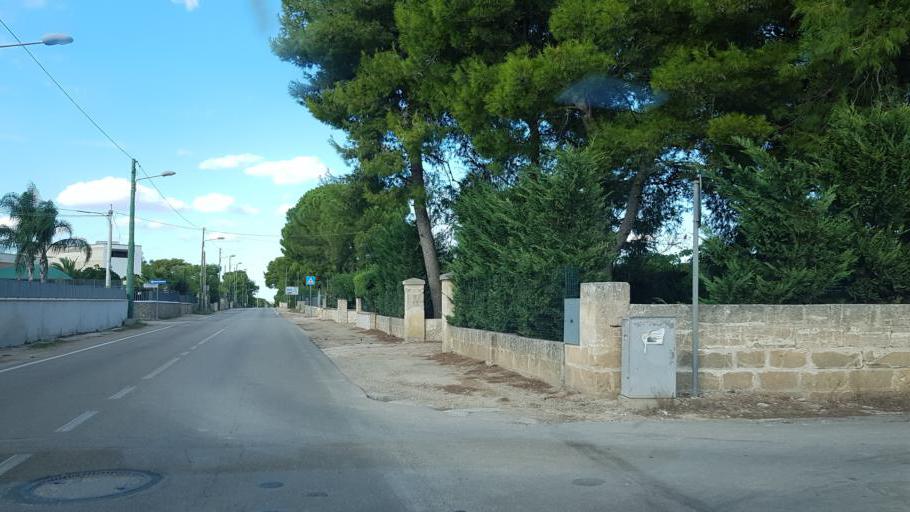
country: IT
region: Apulia
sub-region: Provincia di Lecce
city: Nardo
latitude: 40.1537
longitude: 18.0187
